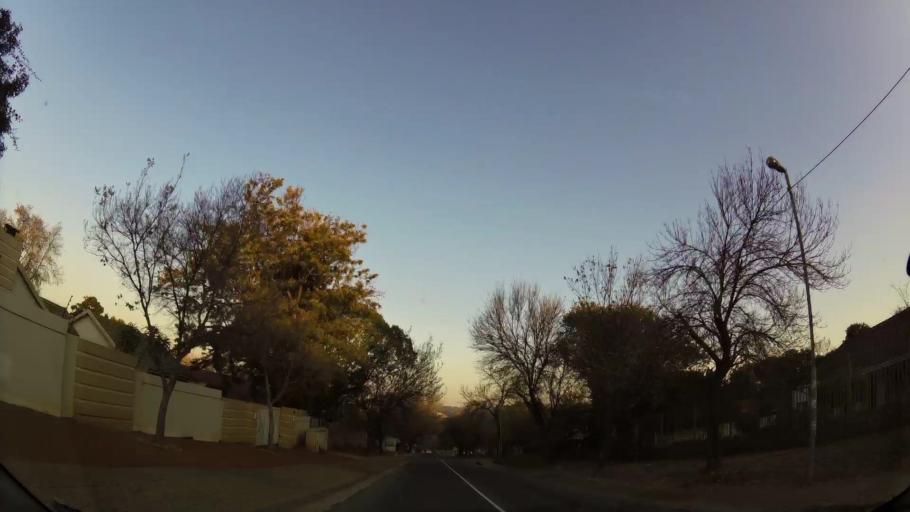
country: ZA
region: Gauteng
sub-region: City of Johannesburg Metropolitan Municipality
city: Johannesburg
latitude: -26.0955
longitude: 28.0117
